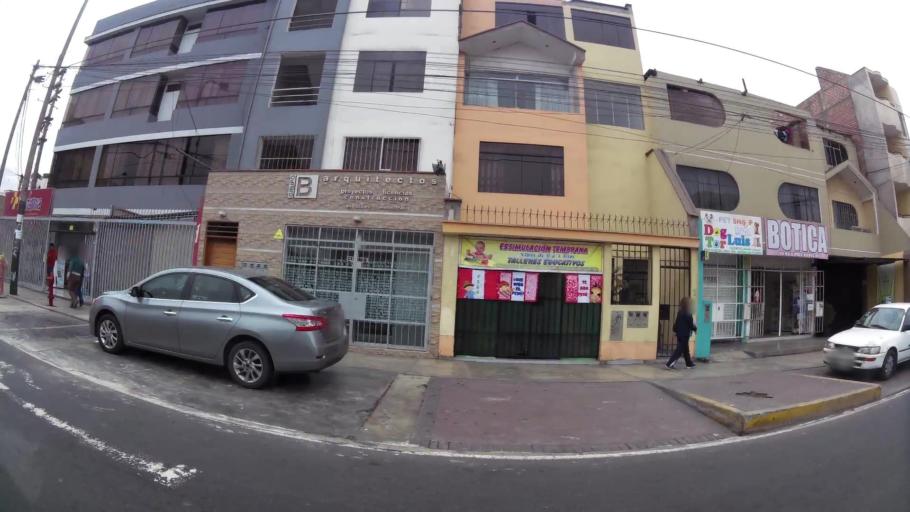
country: PE
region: Lima
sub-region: Lima
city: Surco
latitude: -12.1668
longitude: -76.9905
